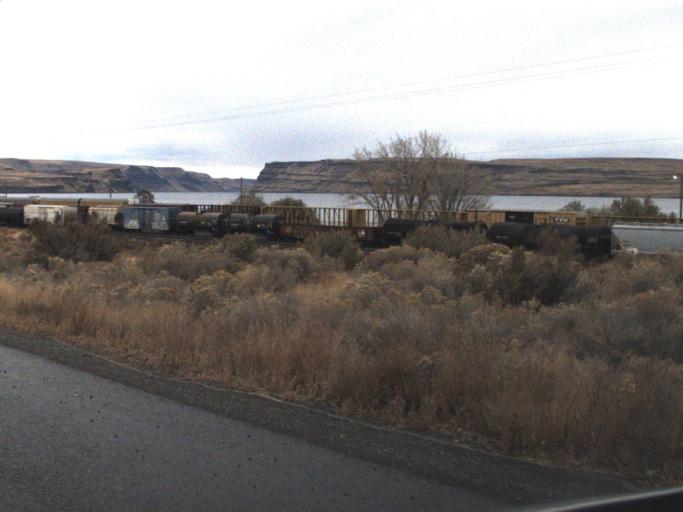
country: US
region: Washington
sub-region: Benton County
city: Finley
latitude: 46.0978
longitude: -118.9122
